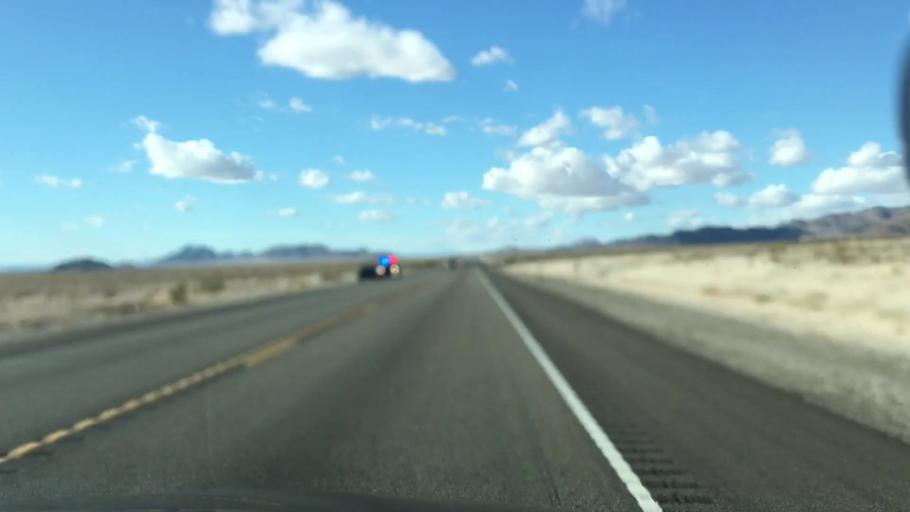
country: US
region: Nevada
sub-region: Nye County
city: Pahrump
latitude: 36.5884
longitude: -116.2196
